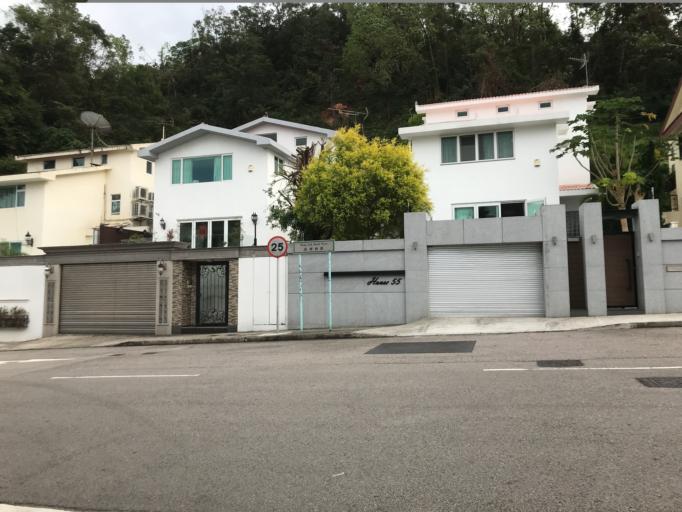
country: HK
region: Tai Po
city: Tai Po
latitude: 22.4606
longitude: 114.1552
